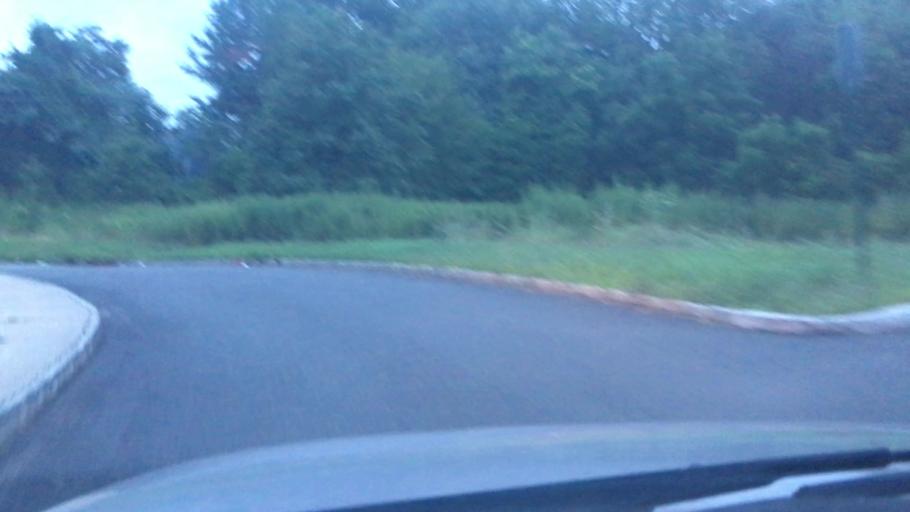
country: US
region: New Jersey
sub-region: Morris County
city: Parsippany
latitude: 40.8479
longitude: -74.4293
